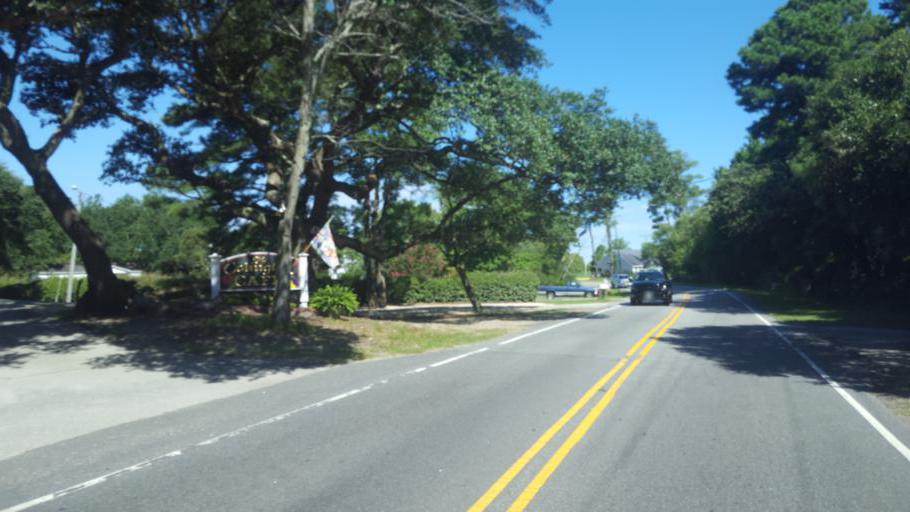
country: US
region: North Carolina
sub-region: Dare County
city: Kill Devil Hills
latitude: 36.0137
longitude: -75.6780
